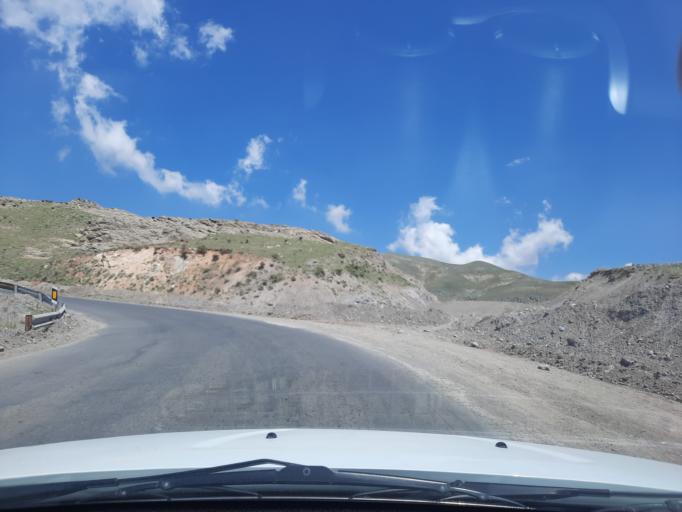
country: IR
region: Qazvin
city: Qazvin
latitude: 36.3706
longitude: 50.2014
